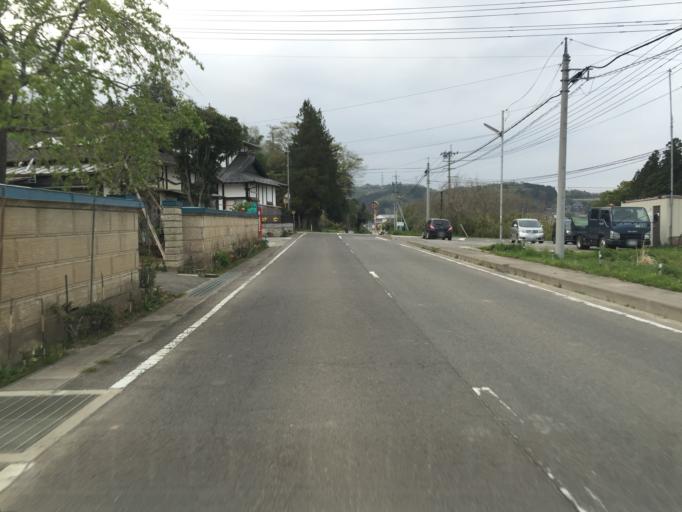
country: JP
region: Fukushima
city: Nihommatsu
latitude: 37.6600
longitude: 140.4235
